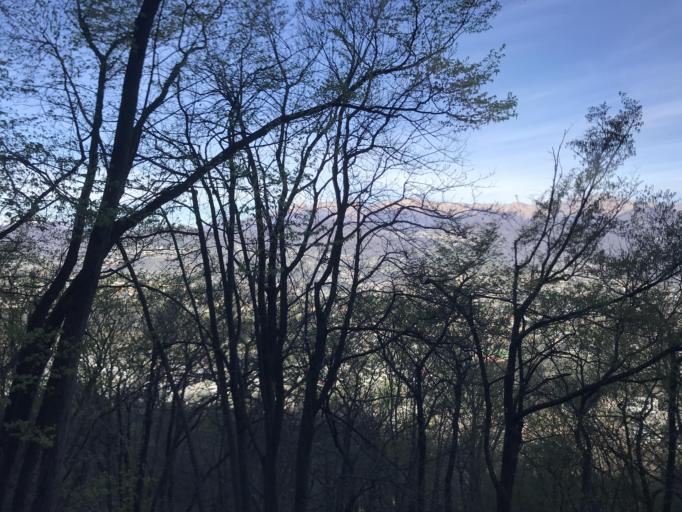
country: CH
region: Ticino
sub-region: Lugano District
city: Sorengo
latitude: 45.9819
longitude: 8.9458
